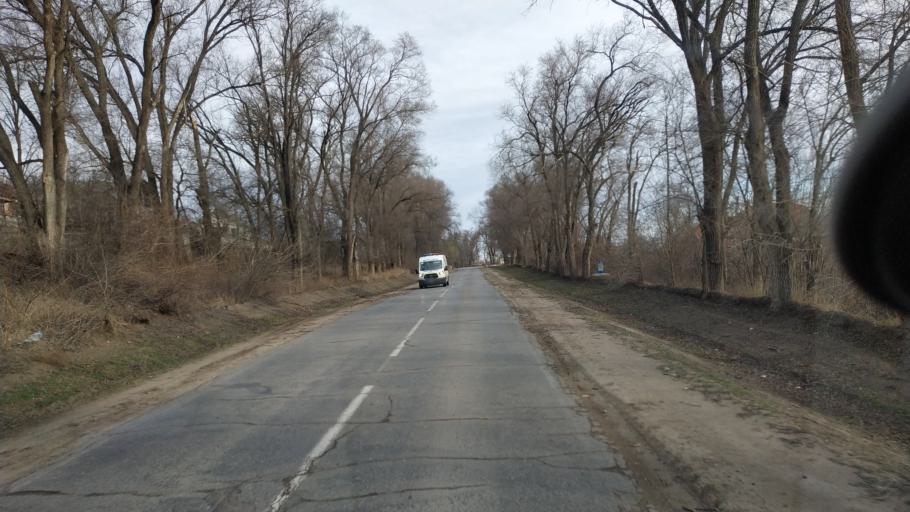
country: MD
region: Chisinau
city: Vadul lui Voda
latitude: 47.1197
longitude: 29.0635
